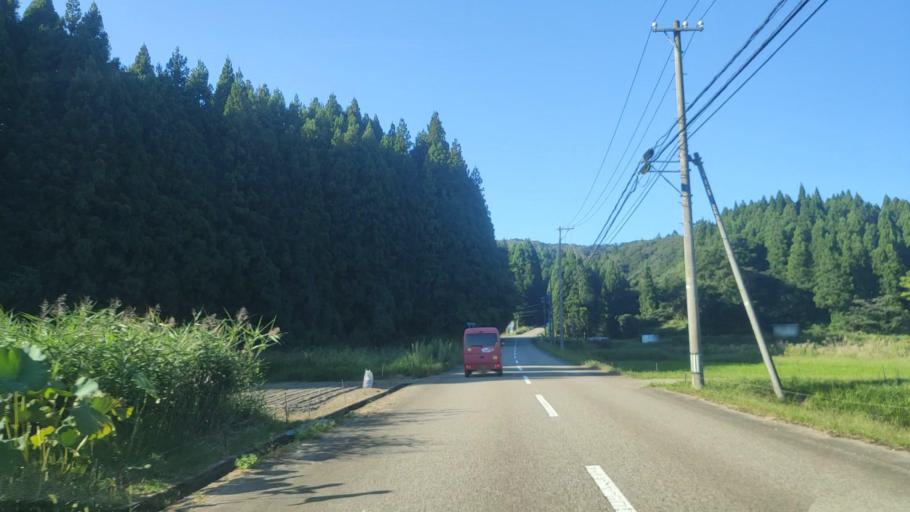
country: JP
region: Ishikawa
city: Nanao
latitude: 37.1077
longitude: 136.9620
